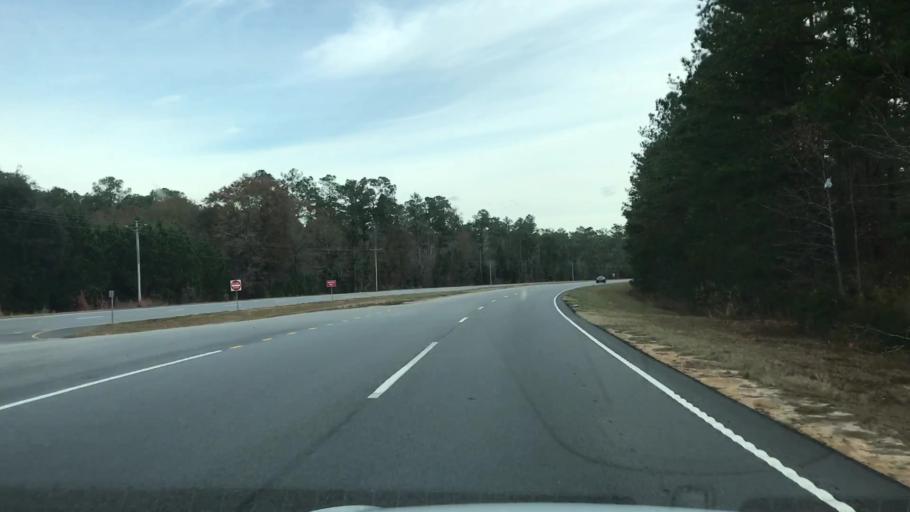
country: US
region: South Carolina
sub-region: Georgetown County
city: Georgetown
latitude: 33.2496
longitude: -79.3750
